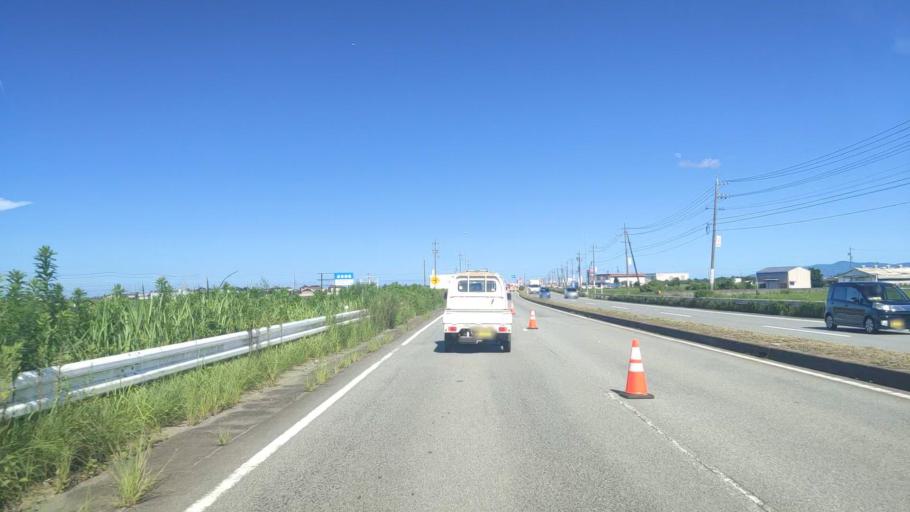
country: JP
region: Mie
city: Ise
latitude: 34.5870
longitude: 136.5995
